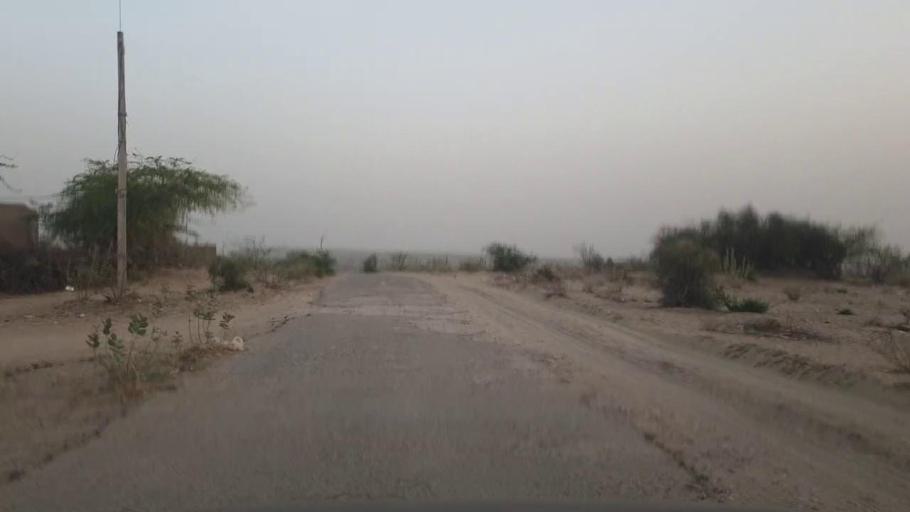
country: PK
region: Sindh
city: Chor
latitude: 25.5120
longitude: 69.8151
